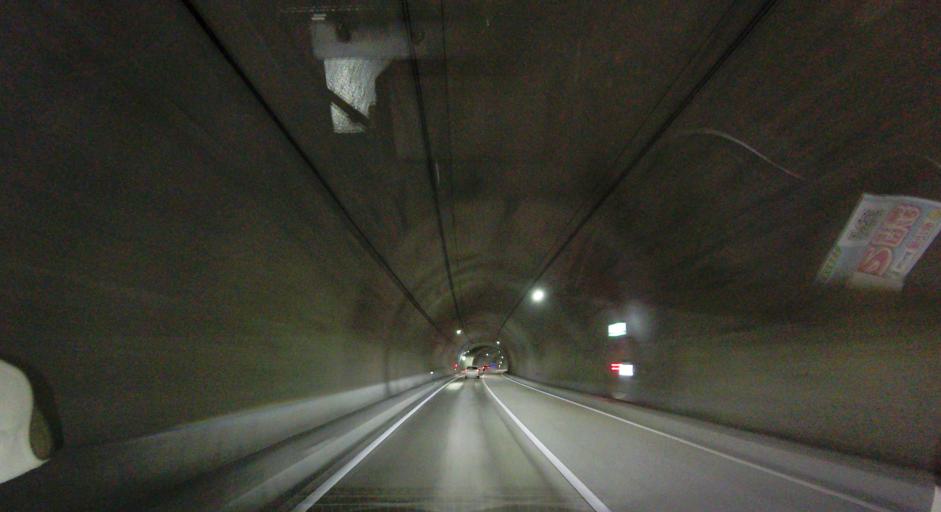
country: JP
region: Miyagi
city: Marumori
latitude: 37.6870
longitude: 140.8248
